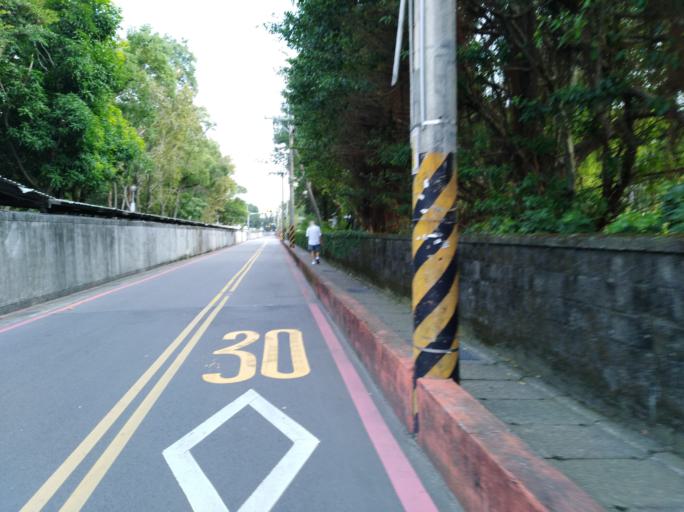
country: TW
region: Taipei
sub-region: Taipei
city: Banqiao
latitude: 25.0359
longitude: 121.4287
